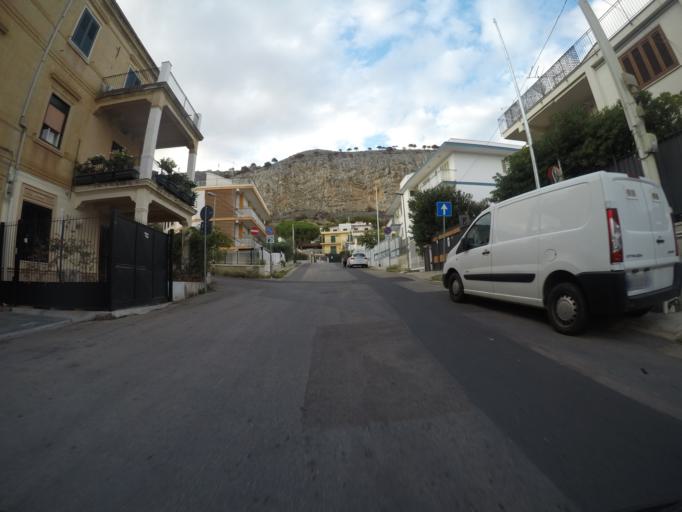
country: IT
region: Sicily
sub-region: Palermo
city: Palermo
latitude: 38.2067
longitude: 13.3235
